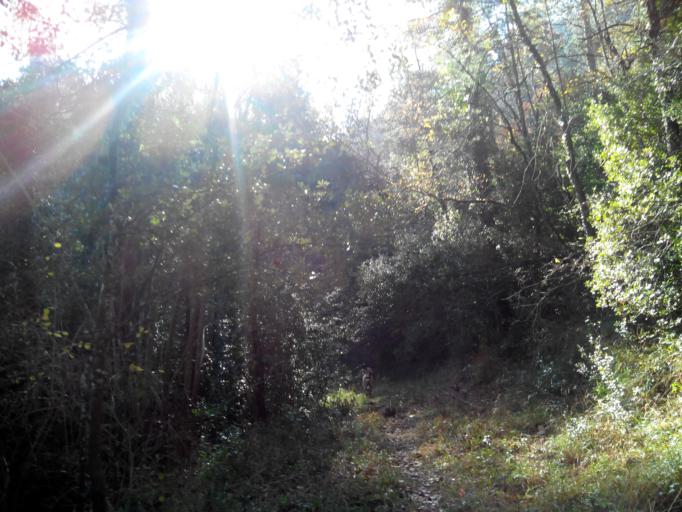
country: ES
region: Catalonia
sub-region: Provincia de Barcelona
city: Vilada
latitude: 42.1107
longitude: 1.9372
